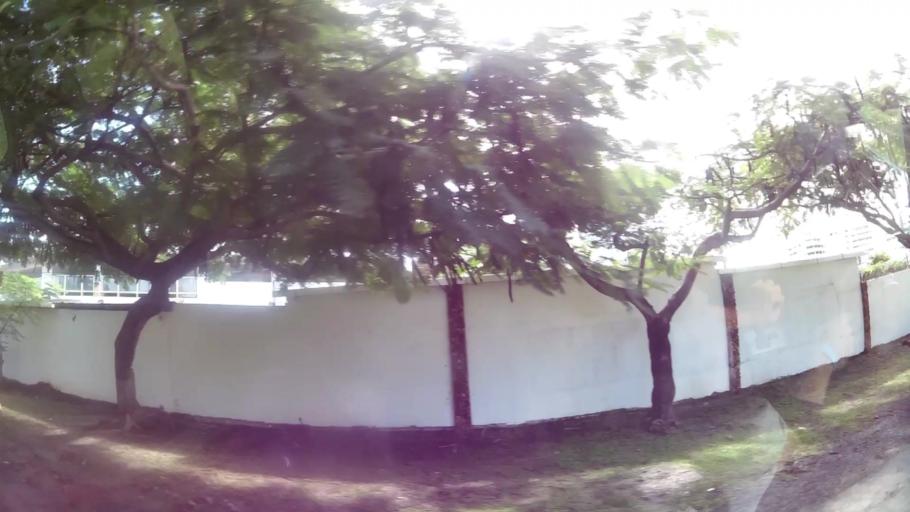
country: PA
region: Panama
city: Nueva Gorgona
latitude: 8.5271
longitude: -79.8930
